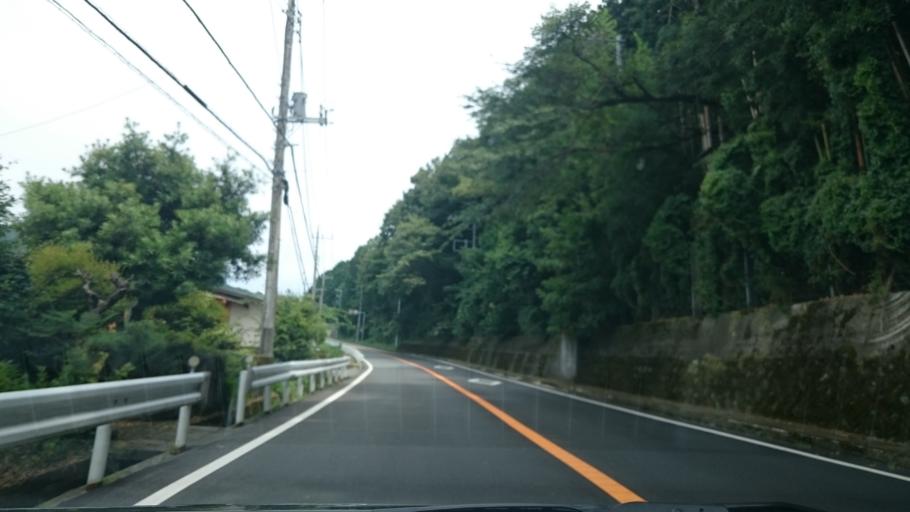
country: JP
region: Shizuoka
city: Mishima
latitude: 35.0055
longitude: 138.9563
